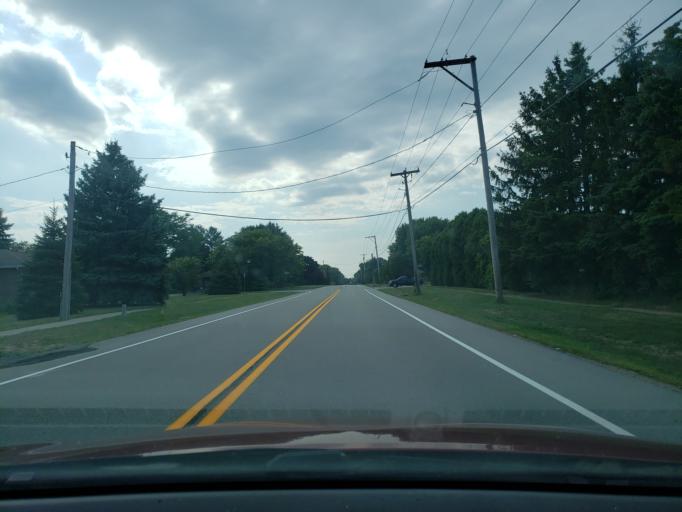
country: US
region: New York
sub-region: Monroe County
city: Greece
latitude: 43.2787
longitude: -77.7045
